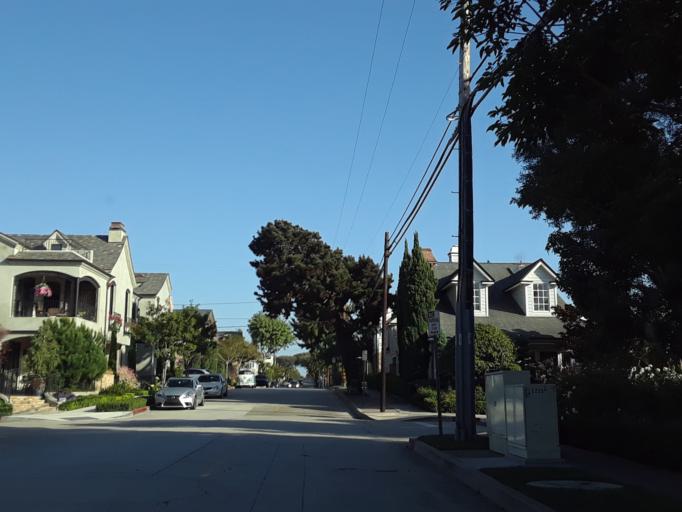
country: US
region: California
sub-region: Orange County
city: San Joaquin Hills
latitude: 33.5962
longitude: -117.8741
